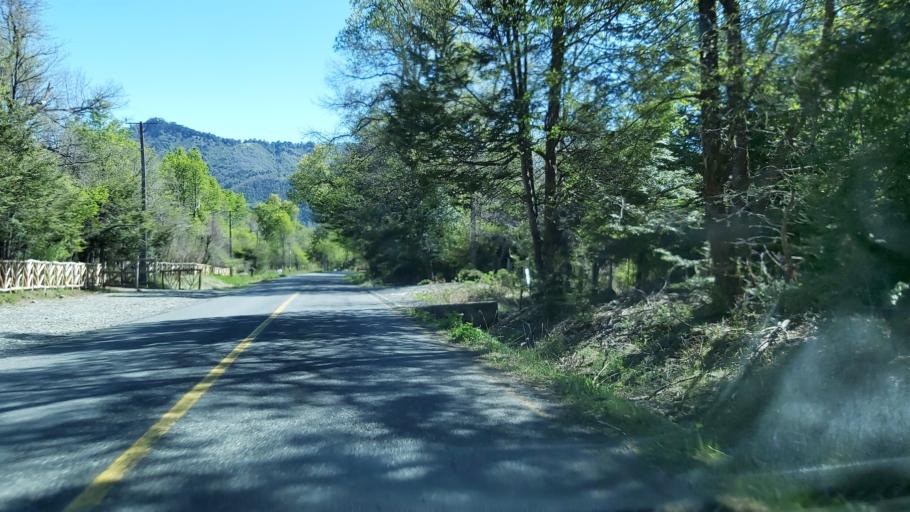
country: CL
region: Araucania
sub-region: Provincia de Cautin
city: Vilcun
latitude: -38.4775
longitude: -71.5335
